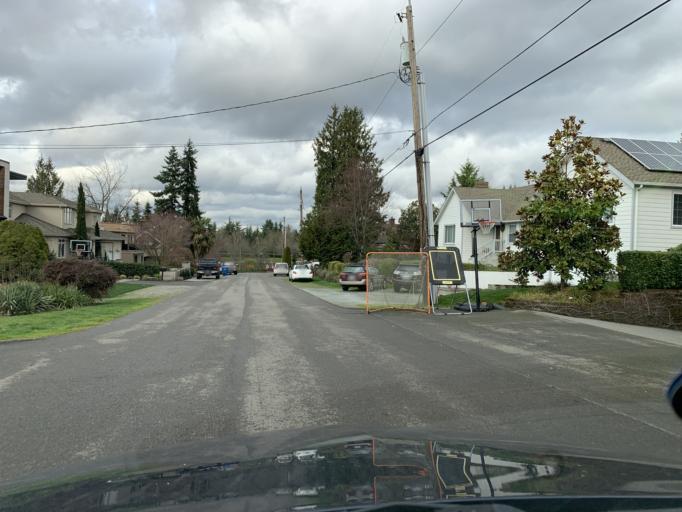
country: US
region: Washington
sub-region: King County
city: Mercer Island
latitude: 47.5902
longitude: -122.2451
